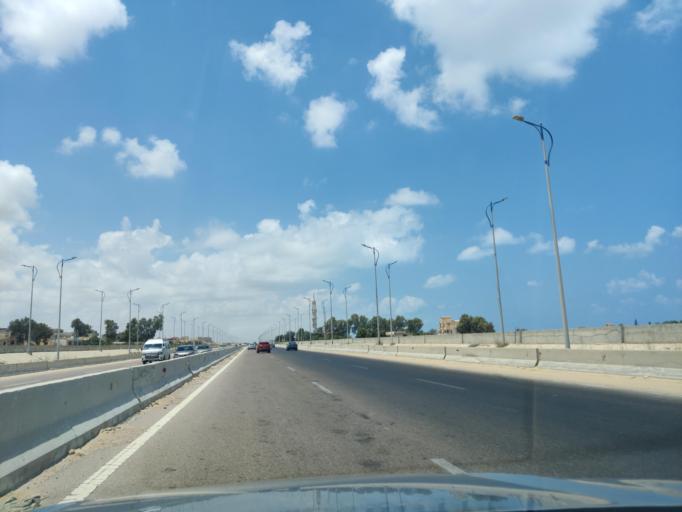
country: EG
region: Alexandria
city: Alexandria
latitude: 30.9539
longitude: 29.5300
